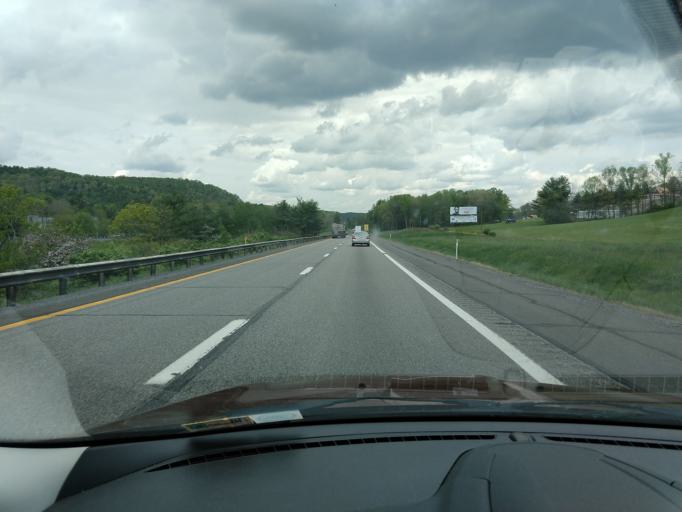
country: US
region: West Virginia
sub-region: Mercer County
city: Athens
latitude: 37.4482
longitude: -81.0646
